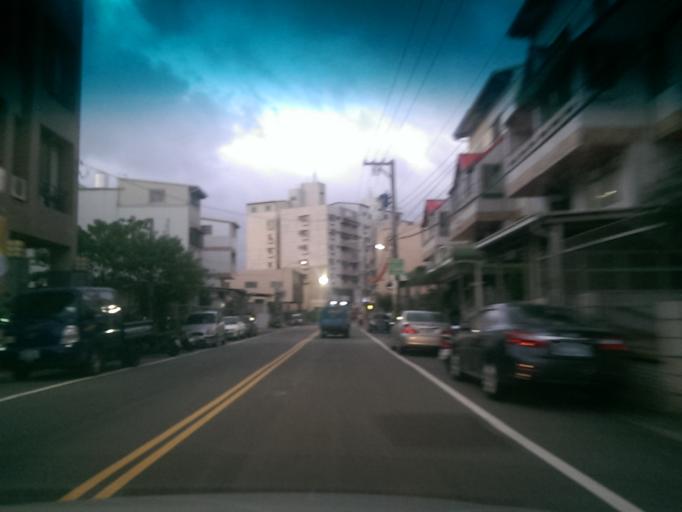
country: TW
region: Taiwan
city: Fengyuan
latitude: 24.2236
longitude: 120.6447
